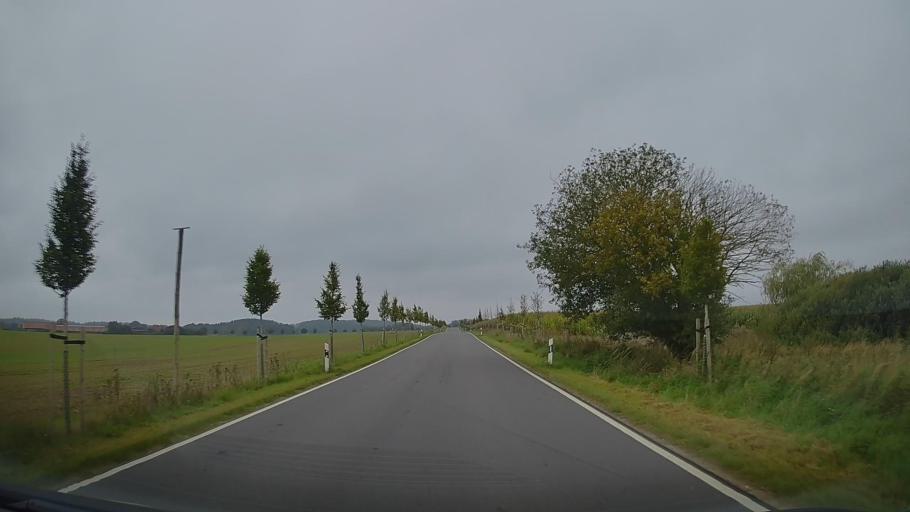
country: DE
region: Mecklenburg-Vorpommern
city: Dummerstorf
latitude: 53.9600
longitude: 12.2370
